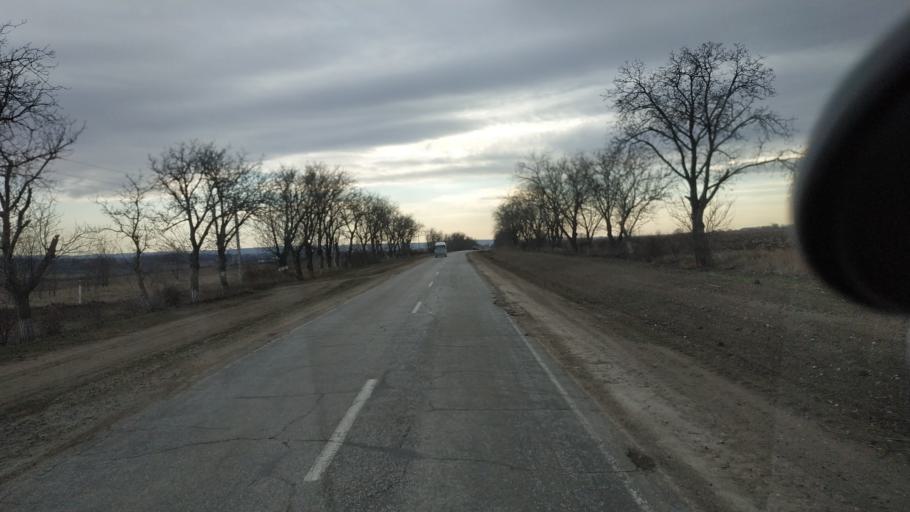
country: MD
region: Criuleni
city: Criuleni
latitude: 47.1789
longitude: 29.1354
